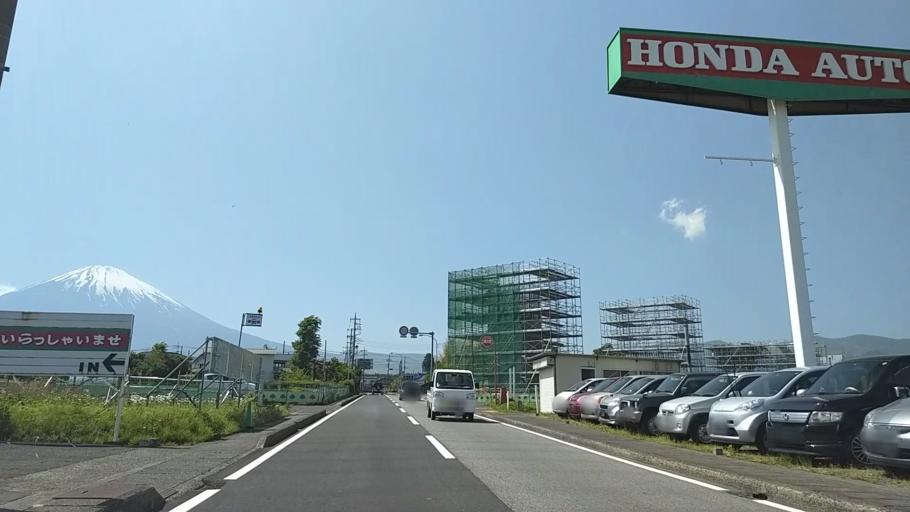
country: JP
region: Shizuoka
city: Gotemba
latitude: 35.3150
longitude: 138.9187
